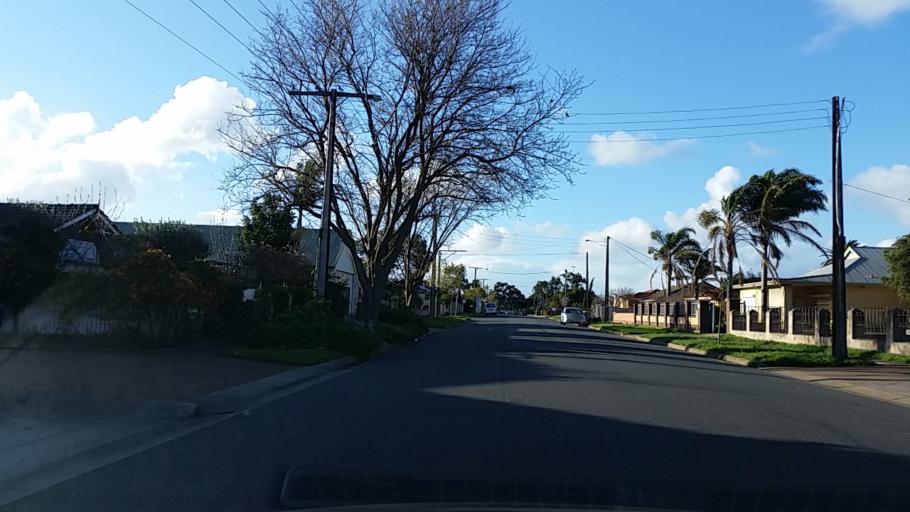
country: AU
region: South Australia
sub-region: Charles Sturt
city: Woodville West
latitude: -34.8903
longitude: 138.5225
